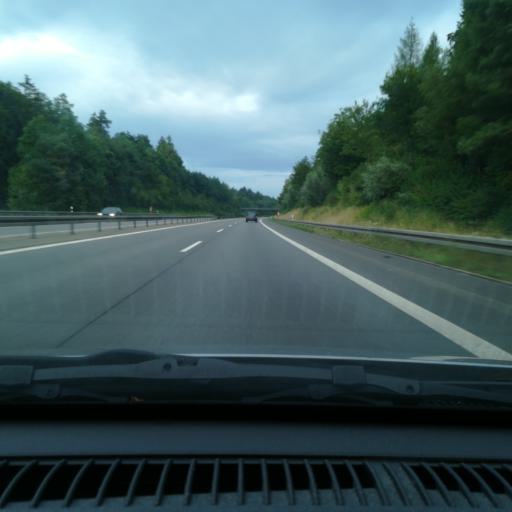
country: DE
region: Baden-Wuerttemberg
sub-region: Freiburg Region
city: Steisslingen
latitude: 47.7713
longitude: 8.9421
